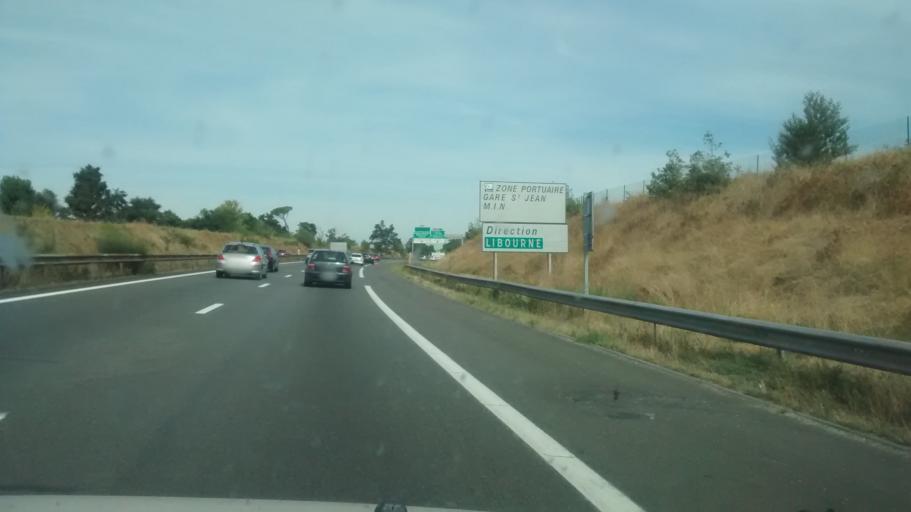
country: FR
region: Aquitaine
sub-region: Departement de la Gironde
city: Villenave-d'Ornon
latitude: 44.7679
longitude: -0.5528
